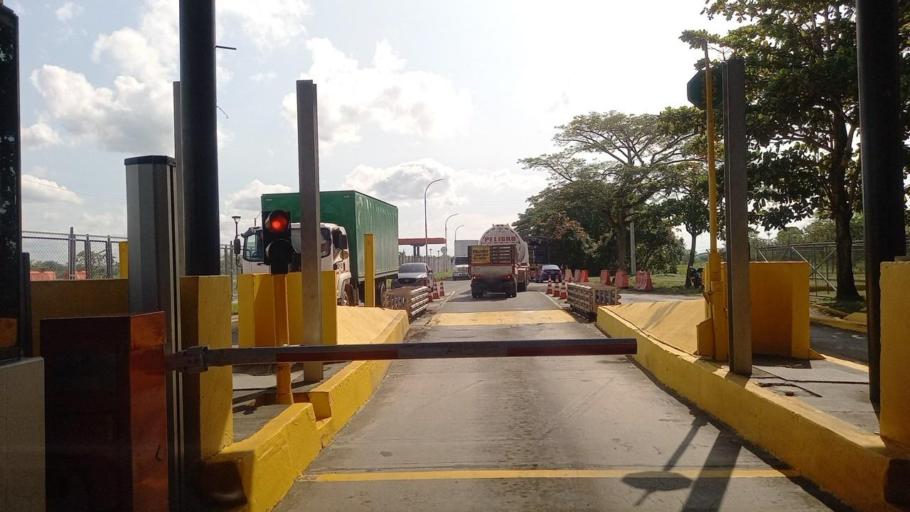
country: CO
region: Antioquia
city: Puerto Berrio
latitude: 6.2948
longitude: -74.4570
